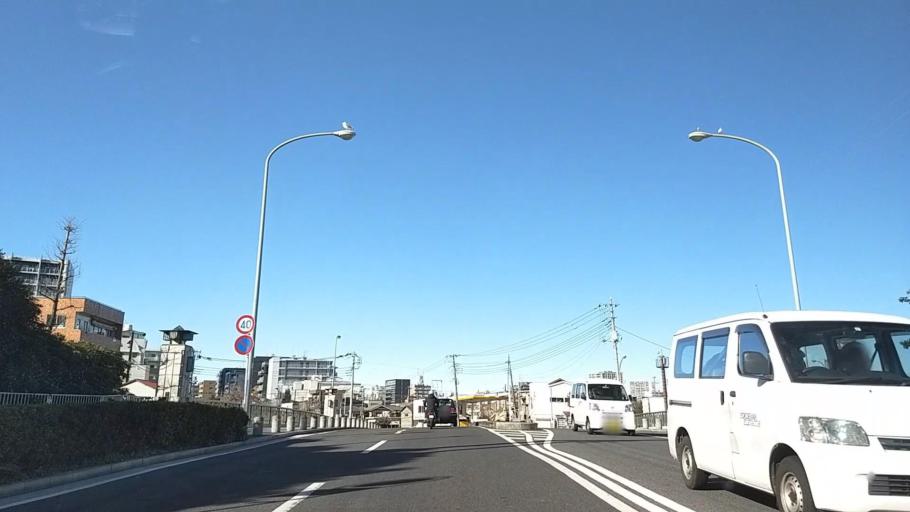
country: JP
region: Kanagawa
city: Yokohama
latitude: 35.4682
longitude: 139.6353
